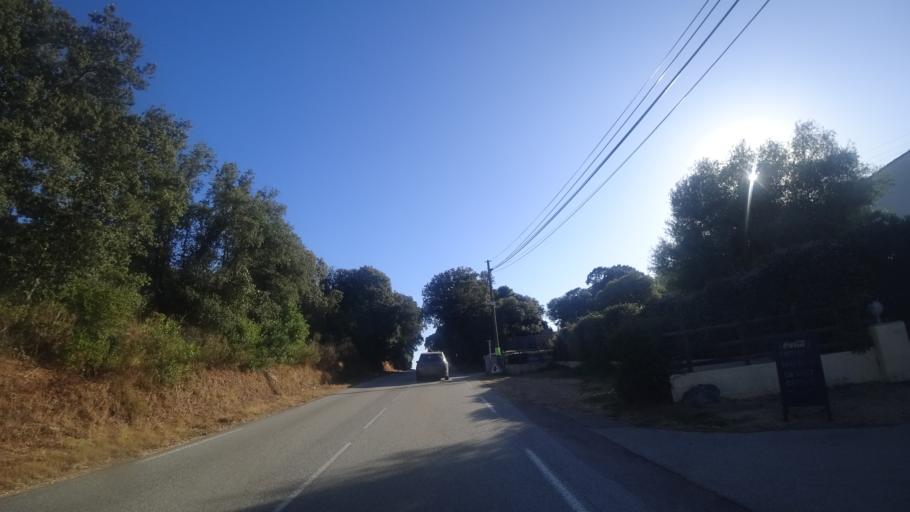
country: FR
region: Corsica
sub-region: Departement de la Corse-du-Sud
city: Cargese
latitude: 42.1624
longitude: 8.5981
